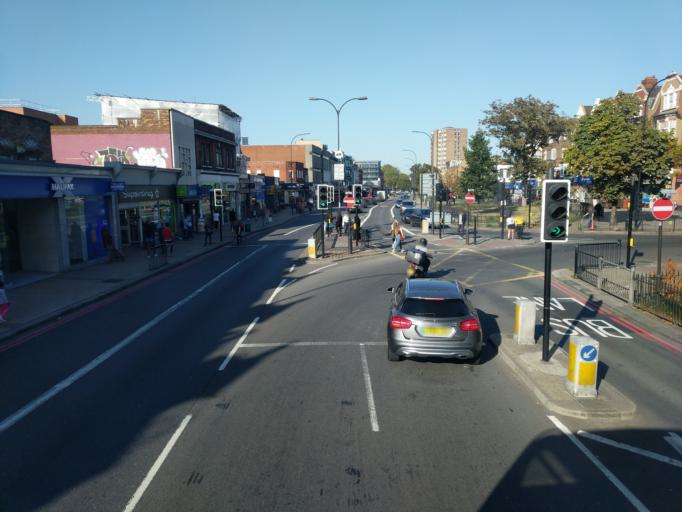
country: GB
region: England
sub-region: Greater London
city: Catford
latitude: 51.4460
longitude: -0.0196
